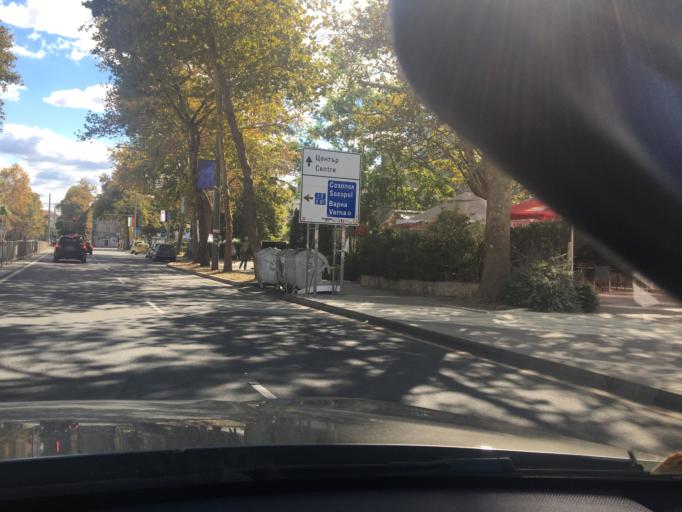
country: BG
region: Burgas
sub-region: Obshtina Burgas
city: Burgas
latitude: 42.5047
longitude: 27.4695
